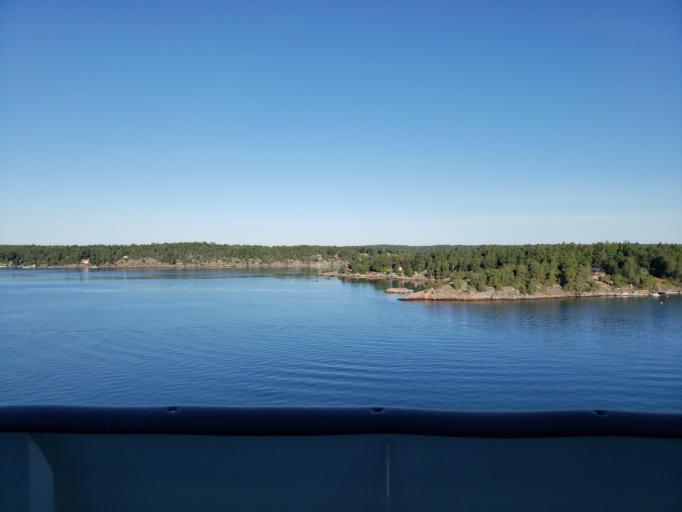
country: SE
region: Stockholm
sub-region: Vaxholms Kommun
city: Vaxholm
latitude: 59.4543
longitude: 18.4300
